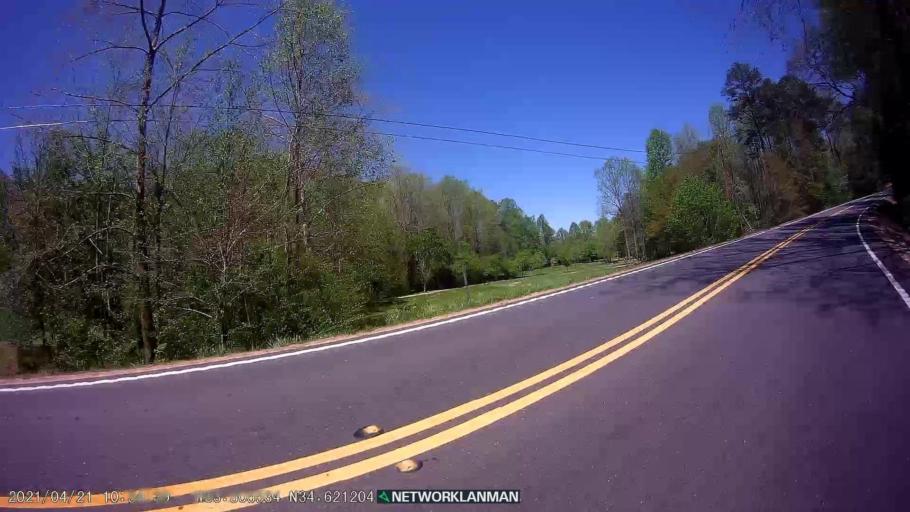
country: US
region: Georgia
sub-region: Habersham County
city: Clarkesville
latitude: 34.6216
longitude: -83.5051
